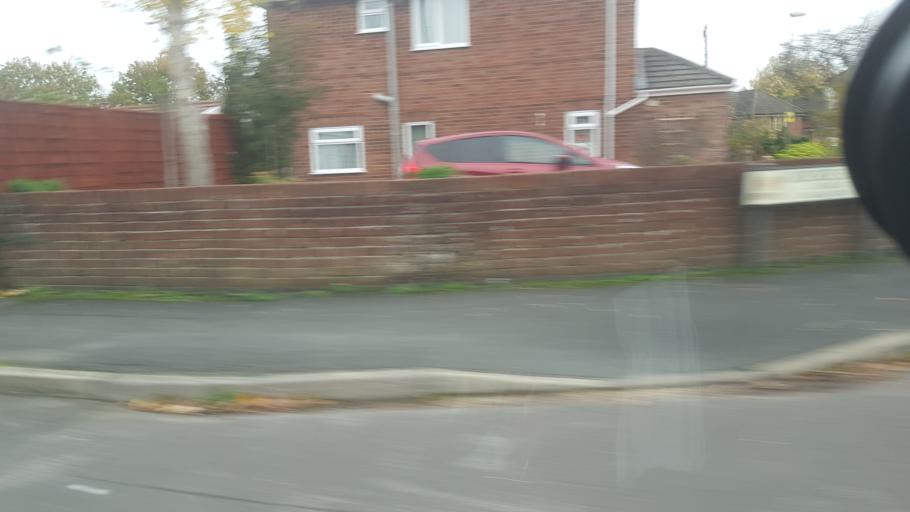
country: GB
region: England
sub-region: Surrey
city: Frimley
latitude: 51.3153
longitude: -0.7664
